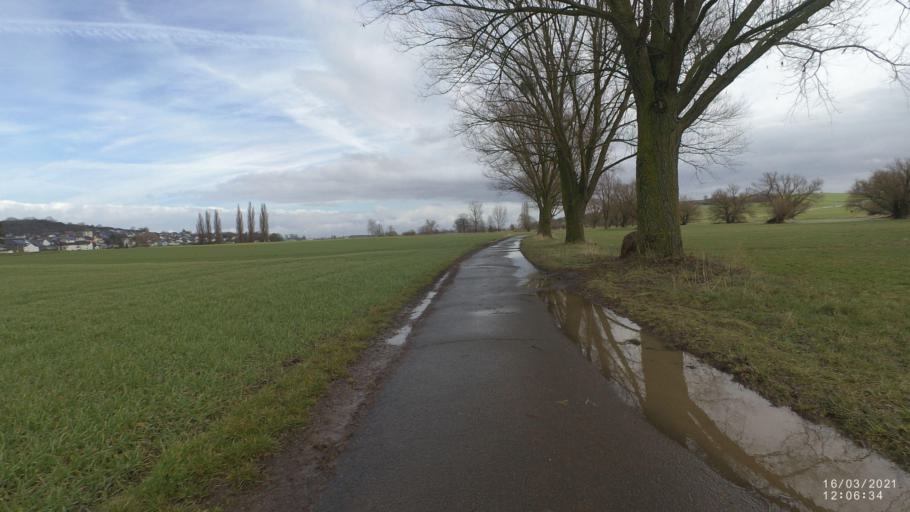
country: DE
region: Rheinland-Pfalz
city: Thur
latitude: 50.3507
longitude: 7.2785
